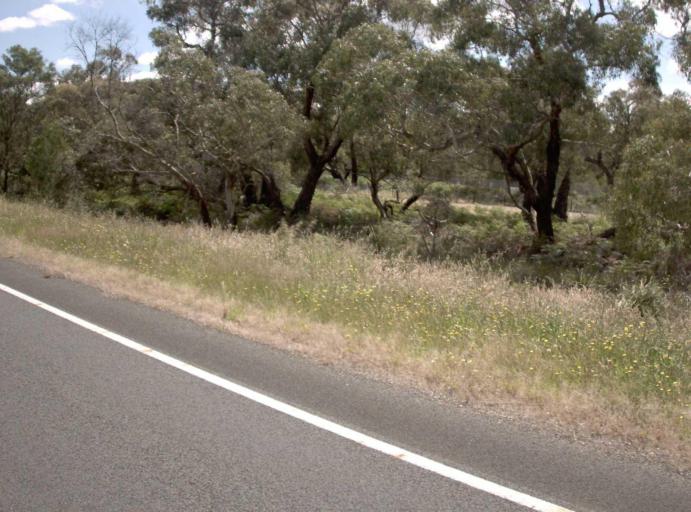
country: AU
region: Victoria
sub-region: Cardinia
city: Koo-Wee-Rup
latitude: -38.3444
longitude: 145.5578
